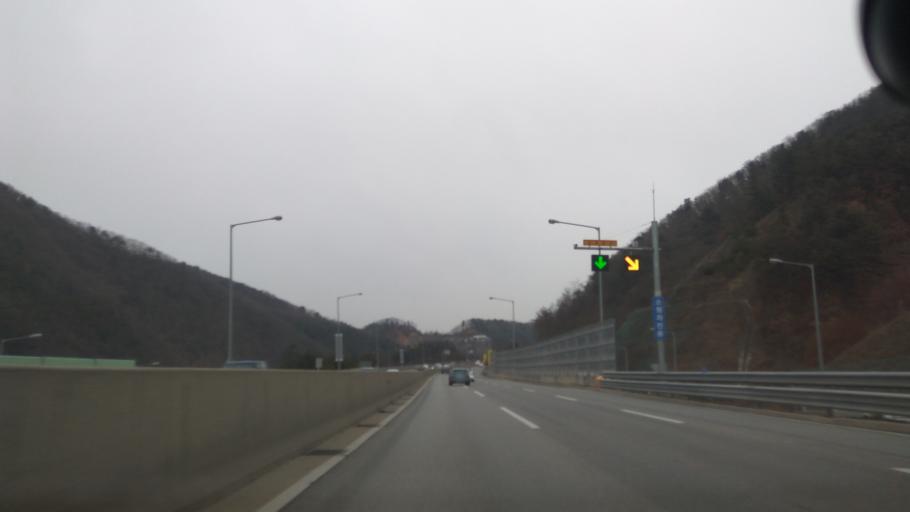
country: KR
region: Gyeonggi-do
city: Hwado
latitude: 37.6341
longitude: 127.3686
